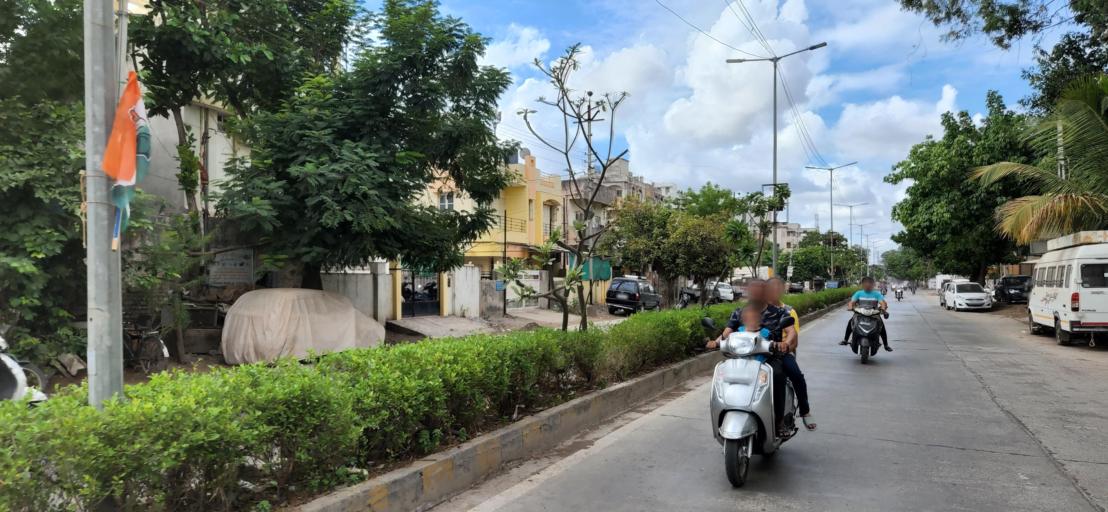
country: IN
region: Gujarat
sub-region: Bhavnagar
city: Bhavnagar
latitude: 21.7499
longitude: 72.1482
